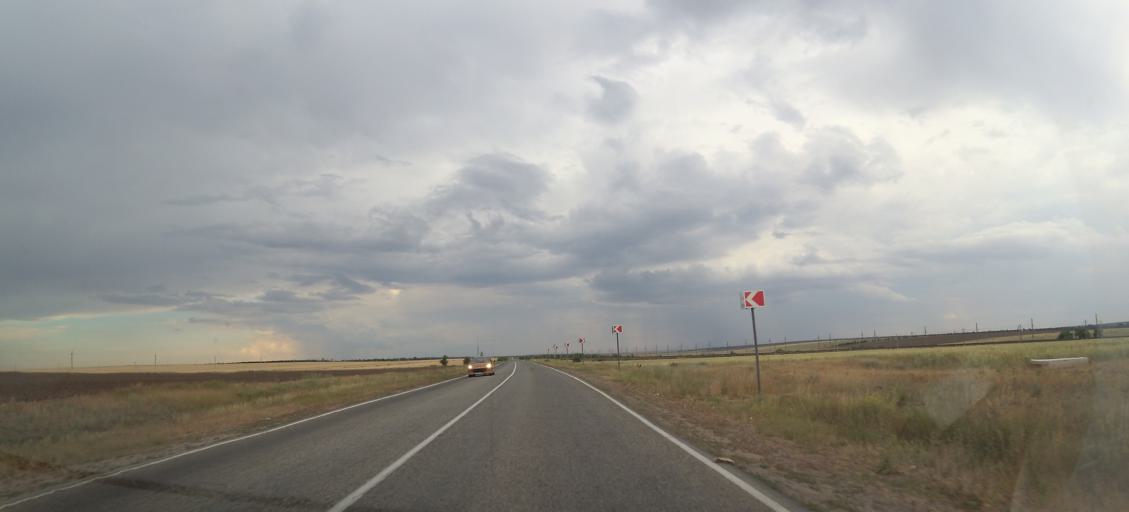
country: RU
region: Rostov
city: Dubovskoye
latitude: 47.4340
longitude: 42.7857
